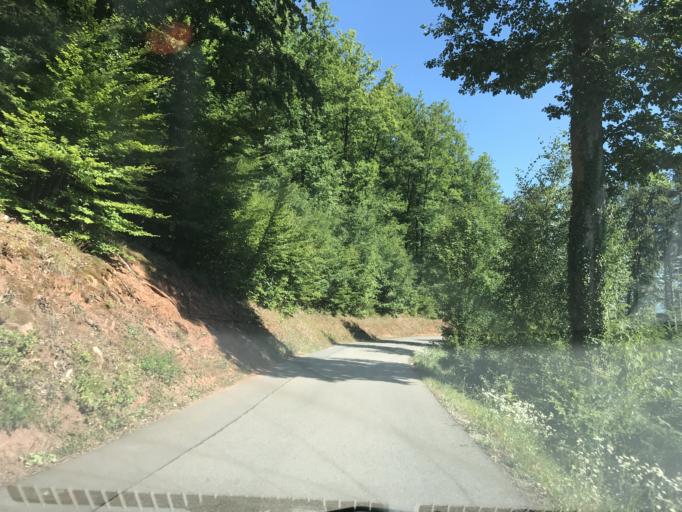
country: DE
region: Baden-Wuerttemberg
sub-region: Freiburg Region
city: Hausen
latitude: 47.6769
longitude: 7.8726
